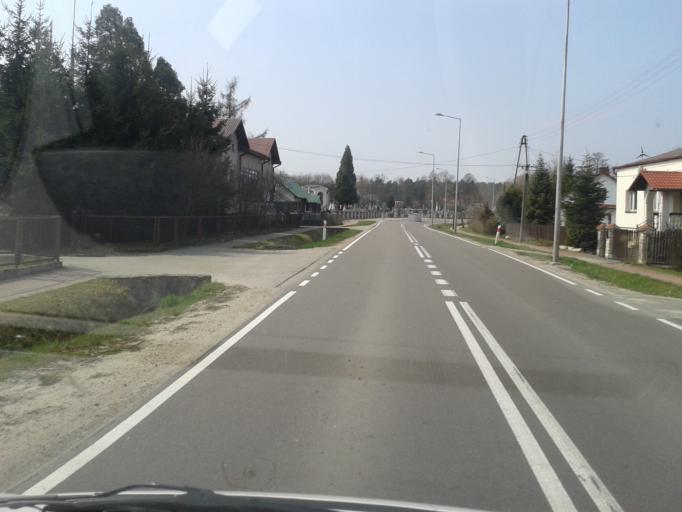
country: PL
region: Subcarpathian Voivodeship
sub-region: Powiat lubaczowski
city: Narol
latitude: 50.3461
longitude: 23.3257
